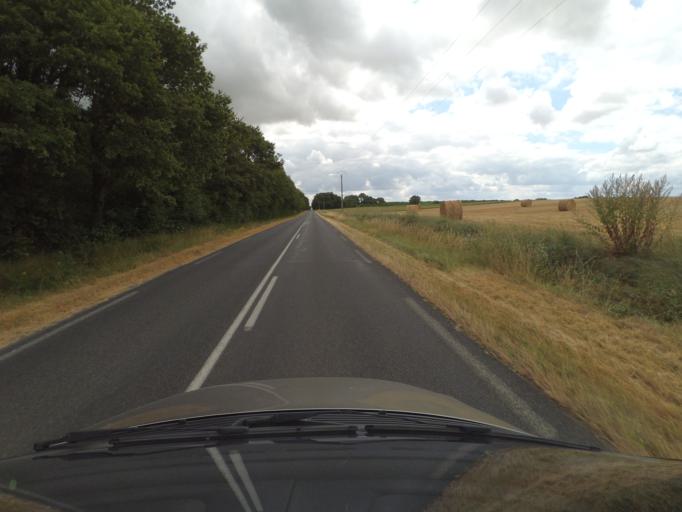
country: FR
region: Centre
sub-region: Departement d'Indre-et-Loire
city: Richelieu
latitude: 46.9851
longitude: 0.3422
